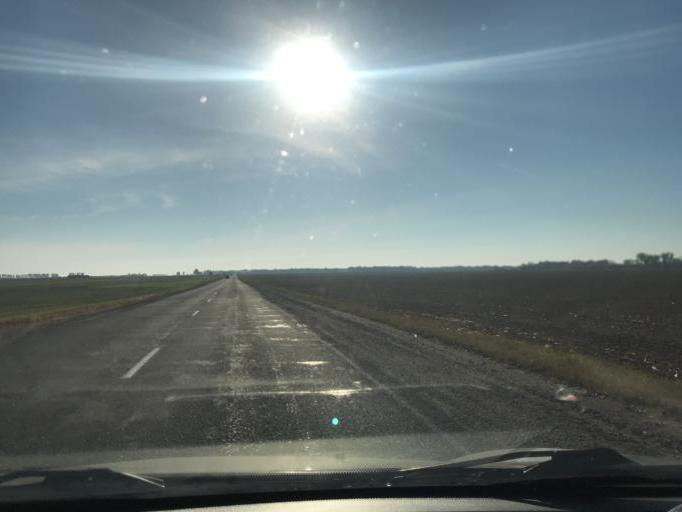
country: BY
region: Gomel
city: Brahin
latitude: 51.8110
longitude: 30.1036
